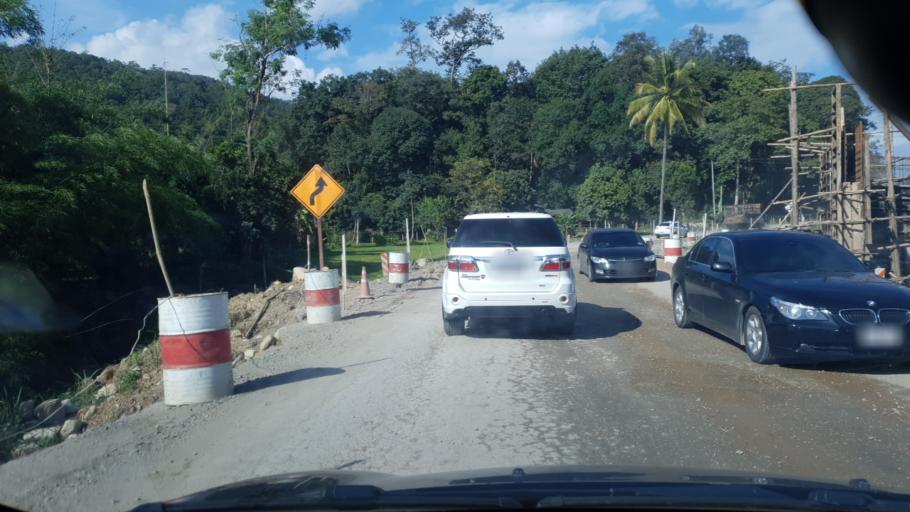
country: TH
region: Chiang Mai
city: Mae On
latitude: 19.0206
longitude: 99.3089
